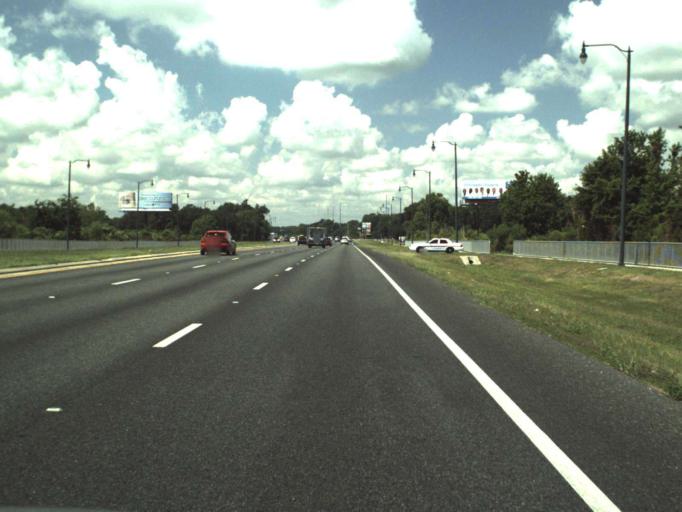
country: US
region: Florida
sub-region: Lake County
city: Silver Lake
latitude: 28.8281
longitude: -81.8267
